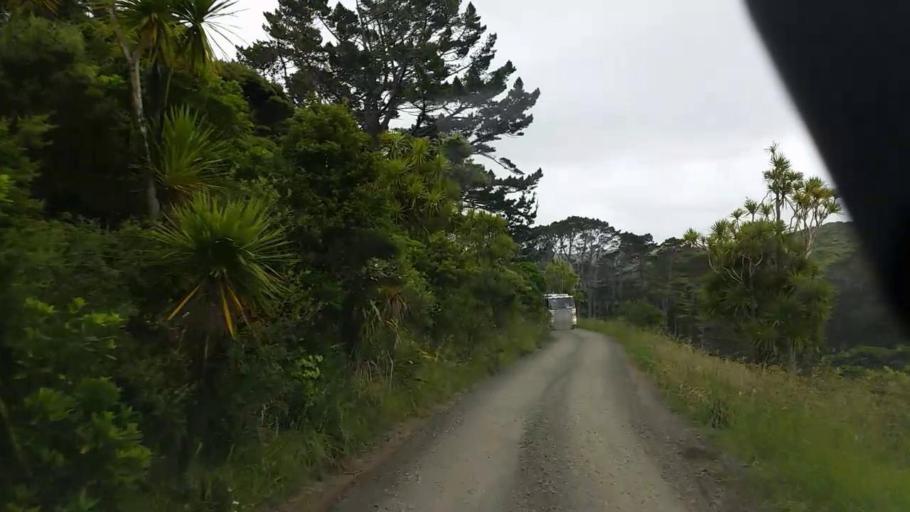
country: NZ
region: Auckland
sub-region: Auckland
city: Muriwai Beach
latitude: -36.9259
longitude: 174.4589
